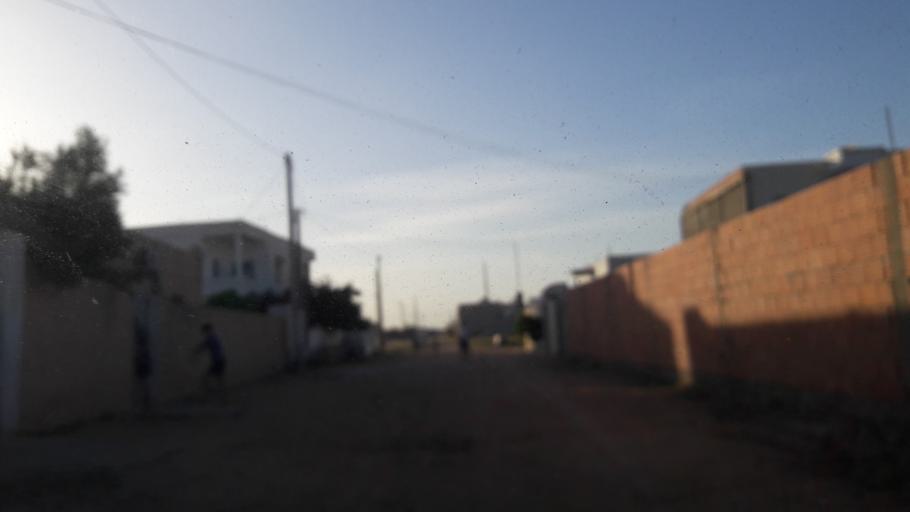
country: TN
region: Safaqis
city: Sfax
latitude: 34.8173
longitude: 10.7418
